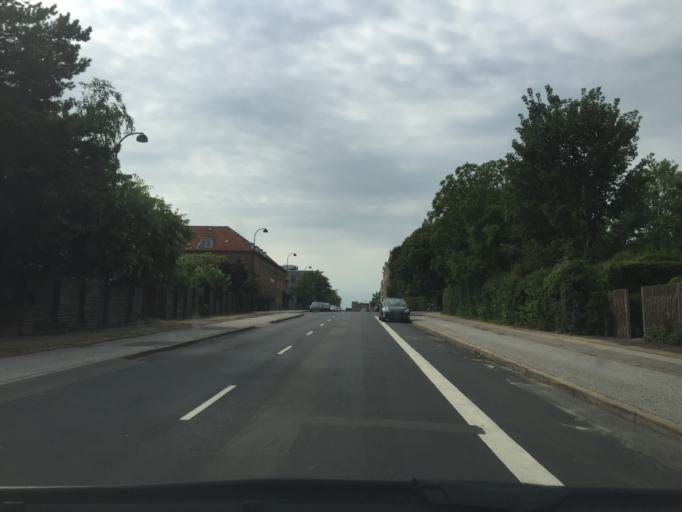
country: DK
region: Capital Region
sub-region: Lyngby-Tarbaek Kommune
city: Kongens Lyngby
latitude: 55.7477
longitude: 12.5446
